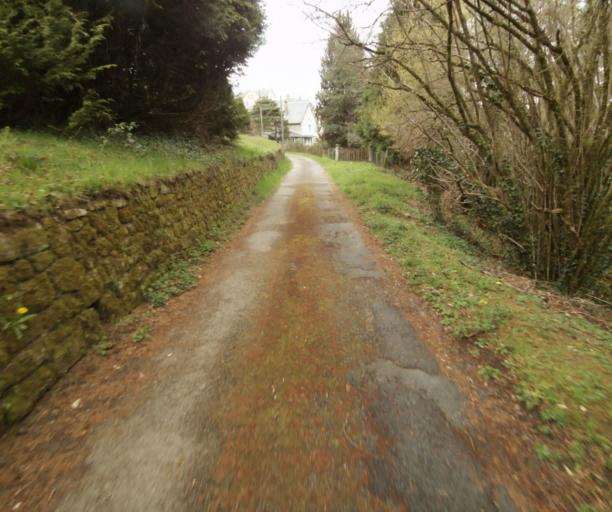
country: FR
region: Limousin
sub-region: Departement de la Correze
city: Argentat
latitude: 45.1938
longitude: 1.9686
